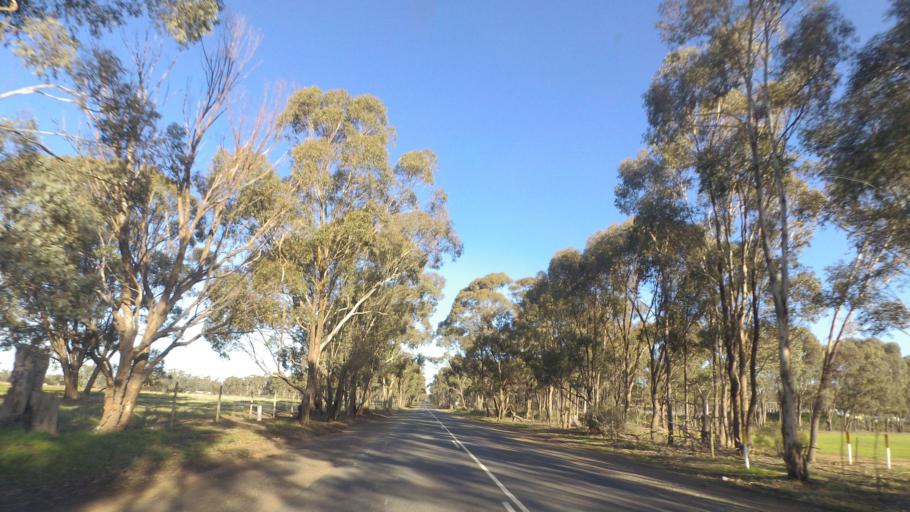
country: AU
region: Victoria
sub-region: Greater Bendigo
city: Epsom
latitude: -36.7363
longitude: 144.5119
